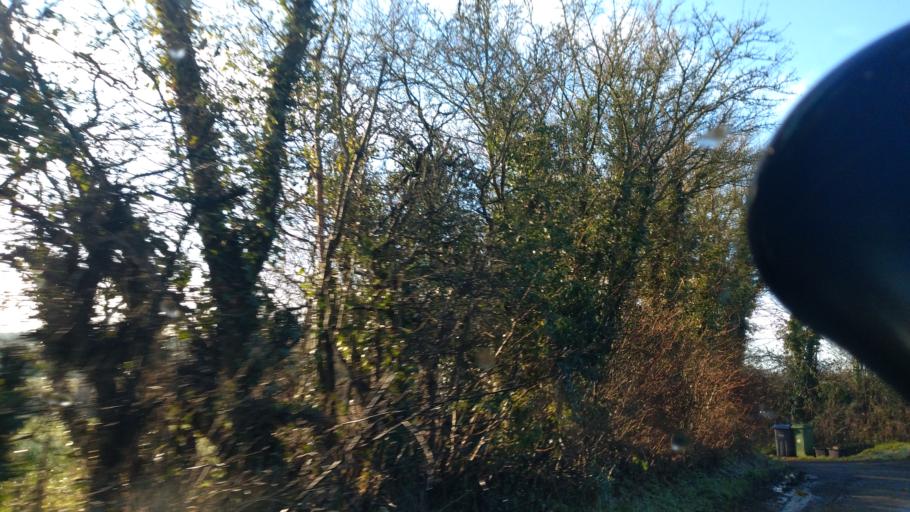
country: GB
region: England
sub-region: Wiltshire
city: Lacock
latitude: 51.4150
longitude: -2.1498
